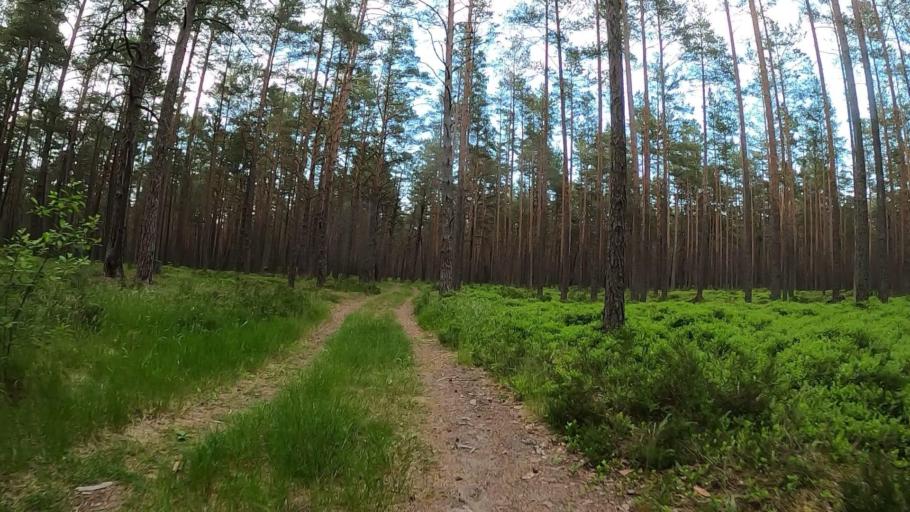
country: LV
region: Carnikava
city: Carnikava
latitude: 57.1536
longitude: 24.2978
